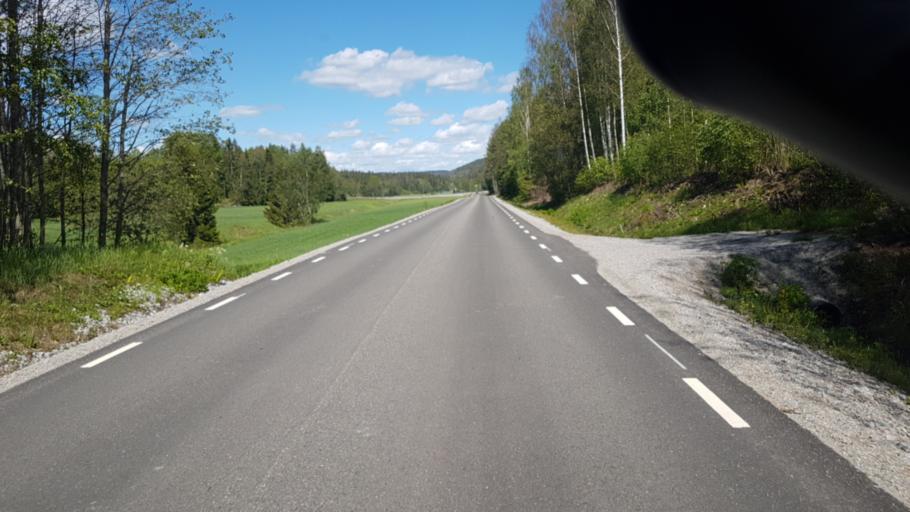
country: SE
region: Vaermland
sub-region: Arvika Kommun
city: Arvika
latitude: 59.6618
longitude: 12.7977
